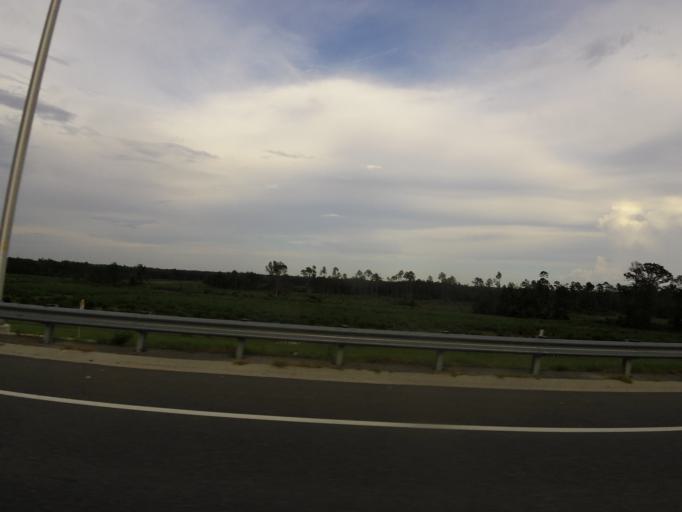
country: US
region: Florida
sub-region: Clay County
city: Lakeside
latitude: 30.1315
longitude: -81.8305
